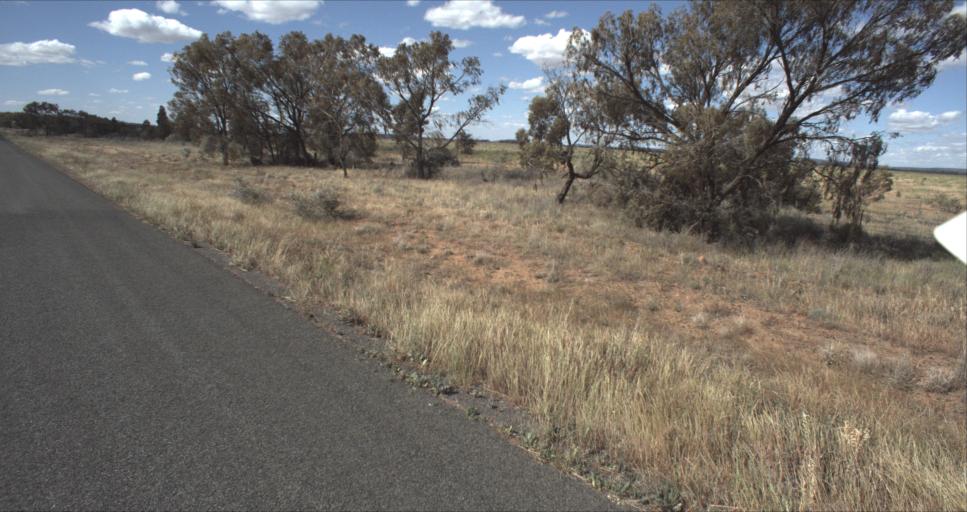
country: AU
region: New South Wales
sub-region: Leeton
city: Leeton
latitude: -34.4353
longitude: 146.2574
